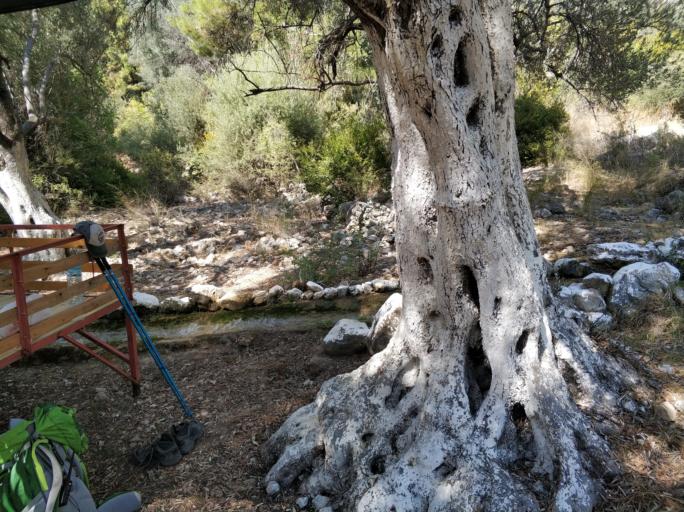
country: TR
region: Antalya
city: Kalkan
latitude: 36.3419
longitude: 29.3973
